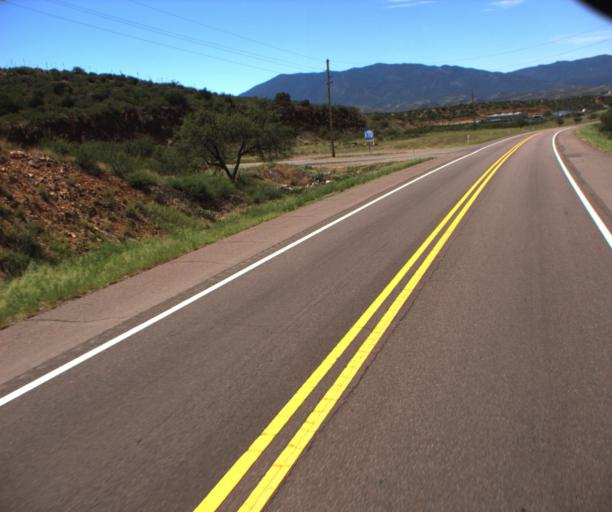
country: US
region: Arizona
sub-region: Gila County
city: Globe
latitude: 33.4008
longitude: -110.7481
